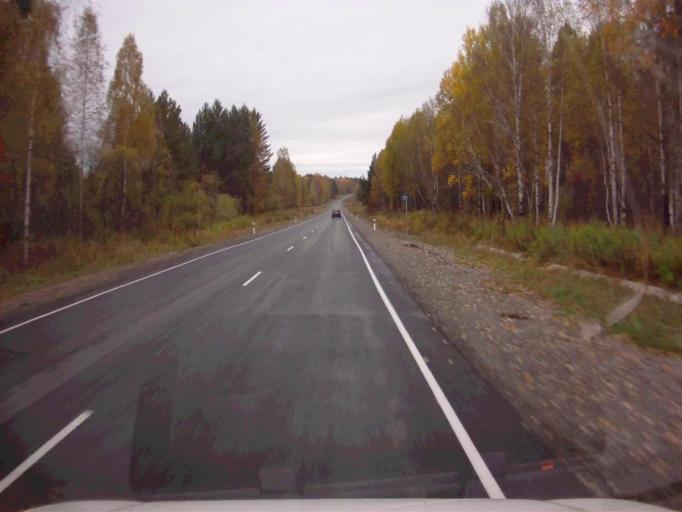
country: RU
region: Chelyabinsk
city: Nyazepetrovsk
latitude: 56.0451
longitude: 59.7591
